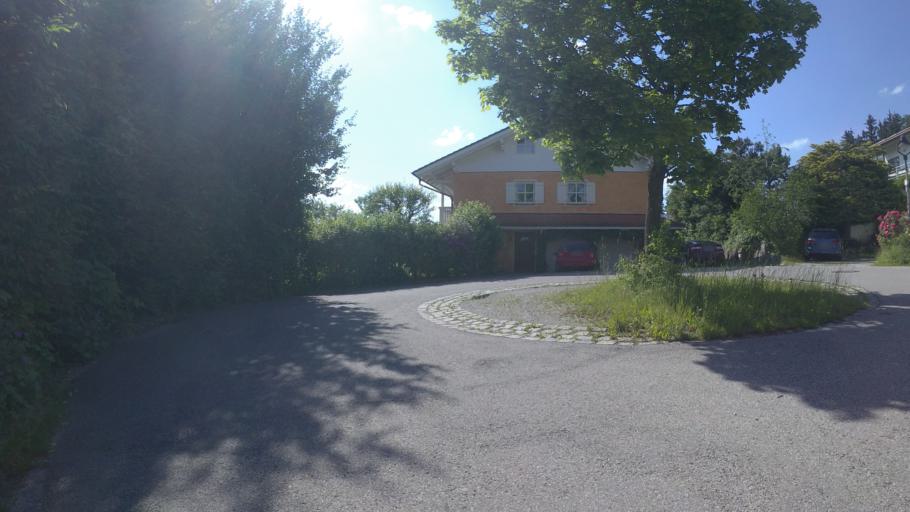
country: DE
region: Bavaria
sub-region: Upper Bavaria
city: Seeon-Seebruck
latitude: 47.9633
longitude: 12.5009
